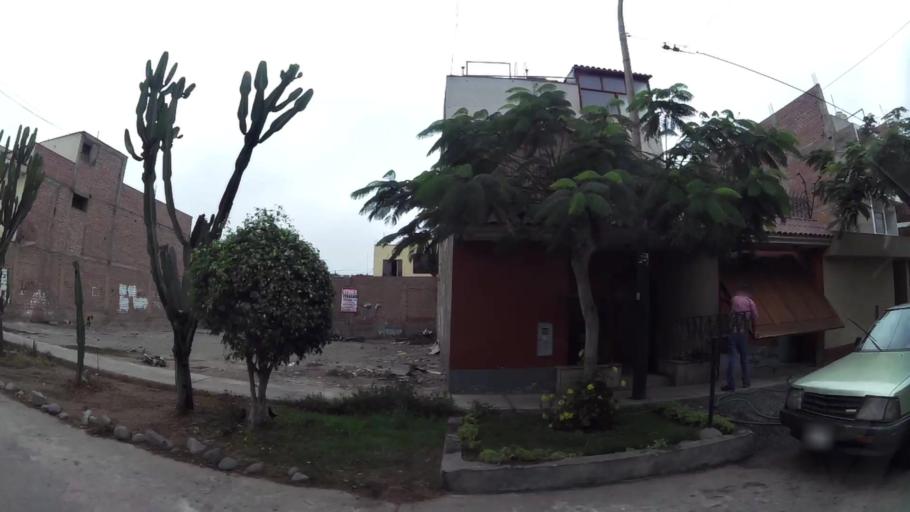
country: PE
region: Lima
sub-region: Lima
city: Surco
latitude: -12.1362
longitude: -76.9850
